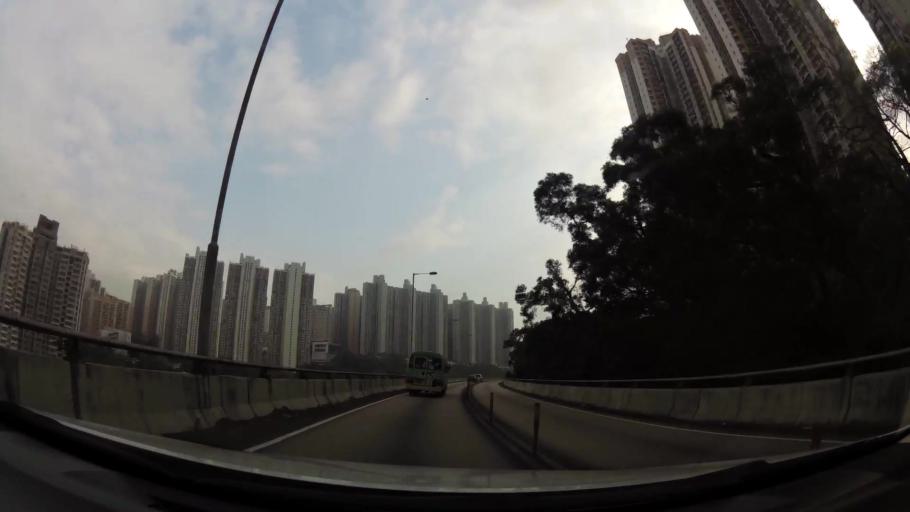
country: HK
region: Kowloon City
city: Kowloon
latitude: 22.3111
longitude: 114.2354
